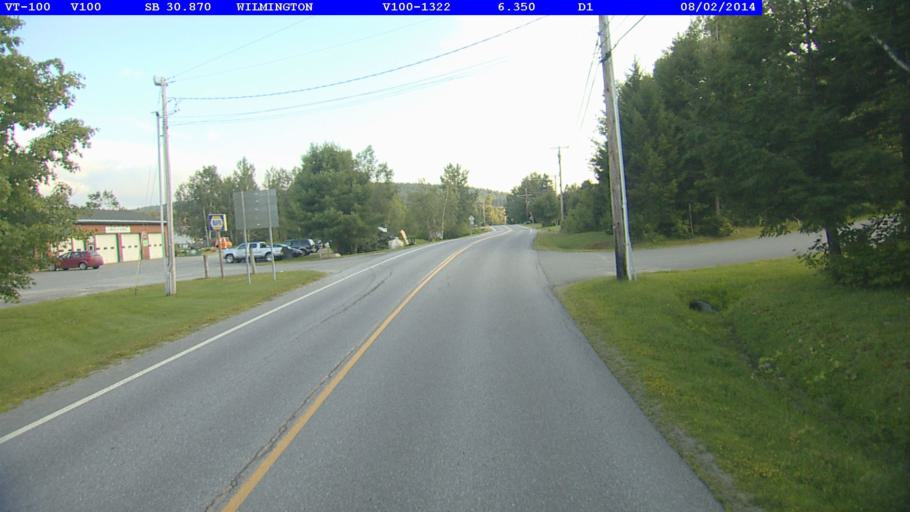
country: US
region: Vermont
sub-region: Windham County
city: Dover
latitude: 42.9128
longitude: -72.8396
